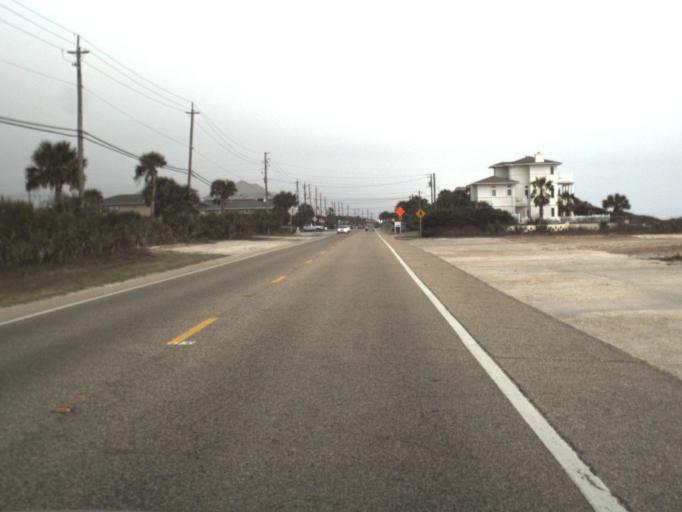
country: US
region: Florida
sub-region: Bay County
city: Laguna Beach
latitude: 30.2567
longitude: -85.9632
